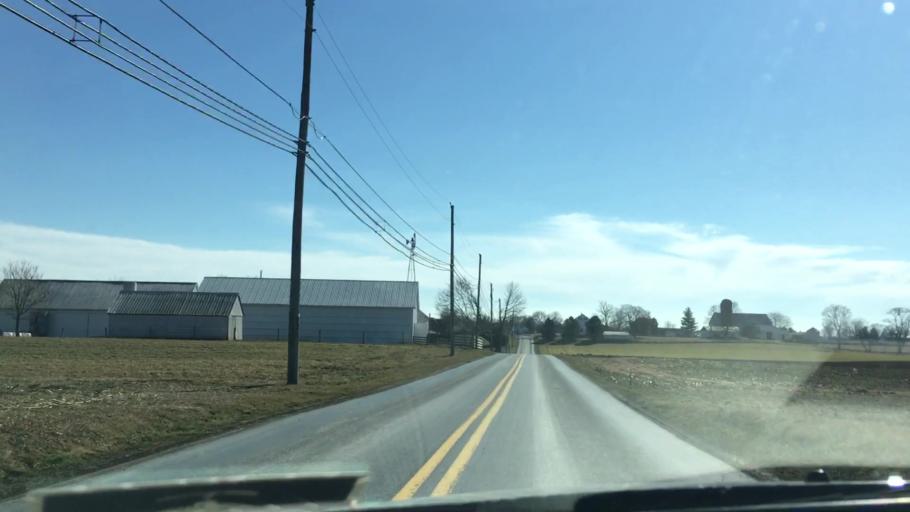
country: US
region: Pennsylvania
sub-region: Lancaster County
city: New Holland
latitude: 40.1328
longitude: -76.1320
